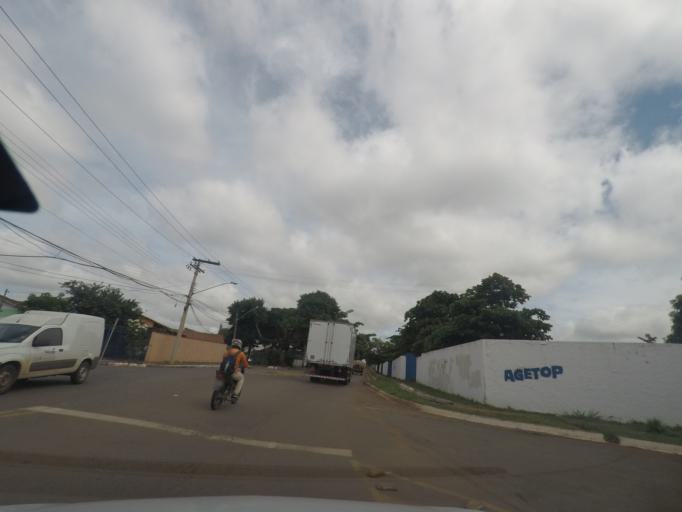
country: BR
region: Goias
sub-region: Goiania
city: Goiania
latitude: -16.6491
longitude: -49.2086
